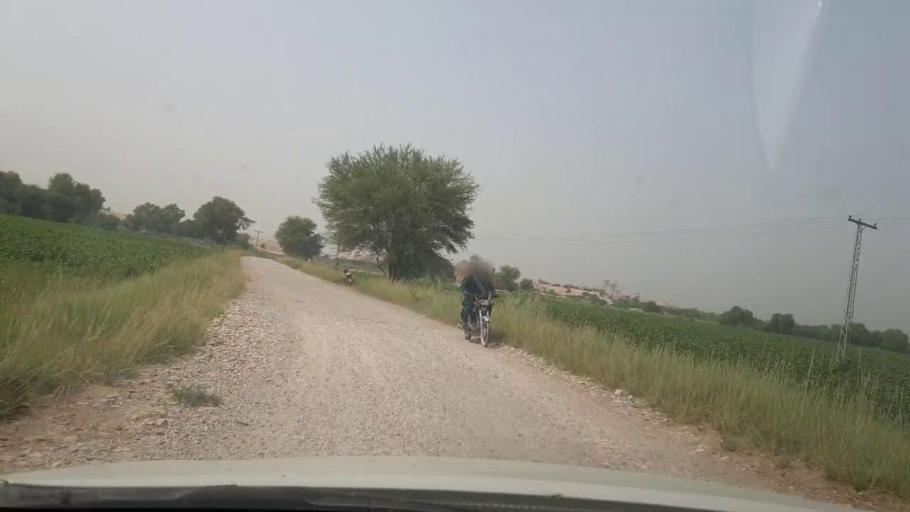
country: PK
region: Sindh
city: Kot Diji
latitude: 27.3104
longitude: 68.6931
